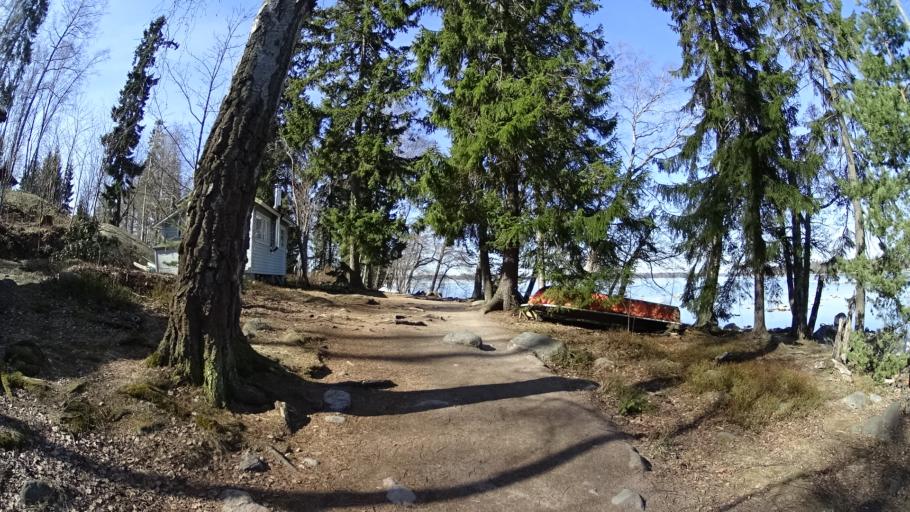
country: FI
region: Uusimaa
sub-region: Helsinki
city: Teekkarikylae
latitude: 60.1467
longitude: 24.8738
